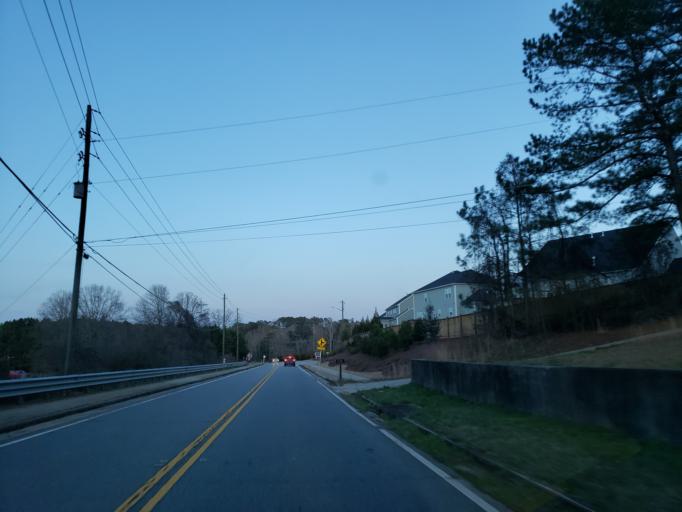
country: US
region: Georgia
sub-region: Cobb County
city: Kennesaw
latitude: 33.9857
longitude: -84.6692
